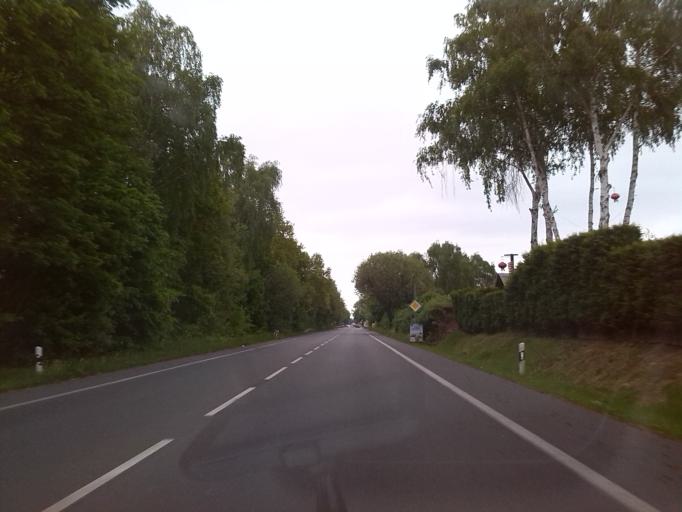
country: DE
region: Hesse
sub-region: Regierungsbezirk Darmstadt
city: Egelsbach
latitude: 49.9654
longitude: 8.6752
